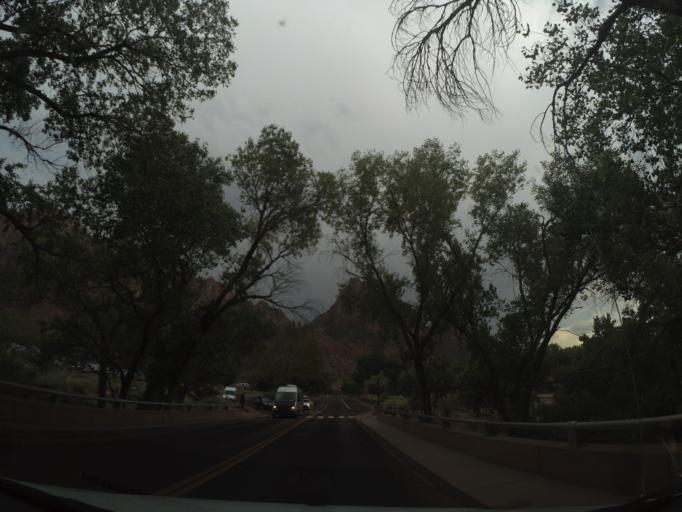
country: US
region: Utah
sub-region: Washington County
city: Hildale
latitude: 37.2016
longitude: -112.9867
